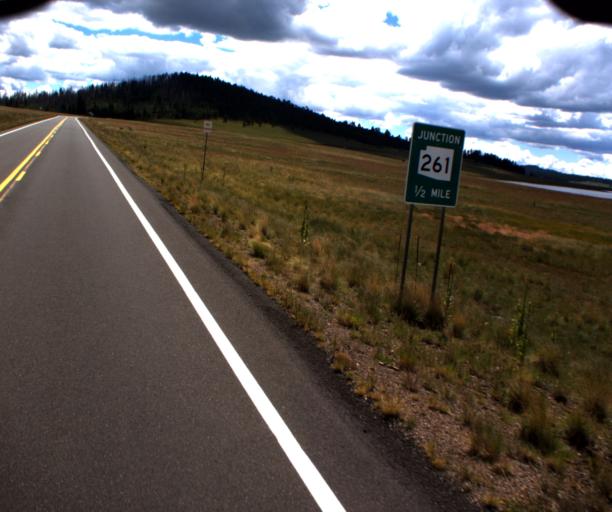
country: US
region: Arizona
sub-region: Apache County
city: Eagar
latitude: 33.9156
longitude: -109.4215
